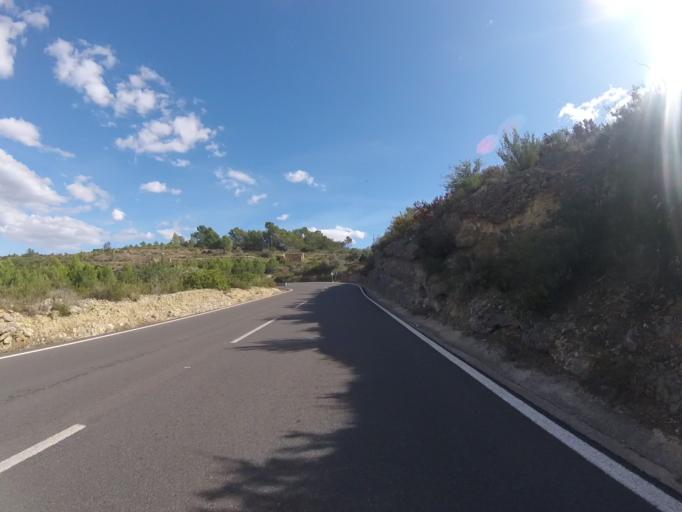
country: ES
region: Valencia
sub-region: Provincia de Castello
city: Cuevas de Vinroma
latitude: 40.3145
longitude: 0.1350
